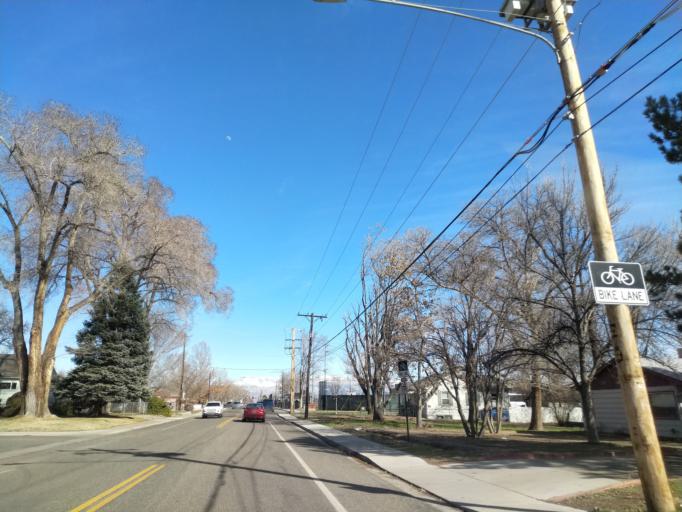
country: US
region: Colorado
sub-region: Mesa County
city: Grand Junction
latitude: 39.0846
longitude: -108.5581
